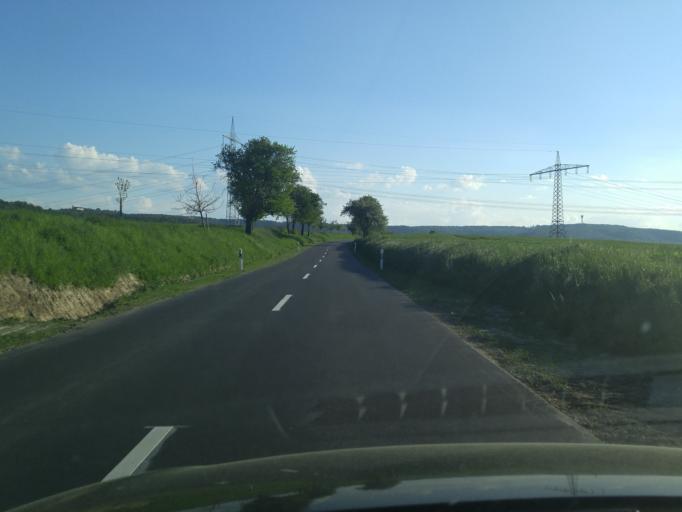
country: DE
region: Baden-Wuerttemberg
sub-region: Regierungsbezirk Stuttgart
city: Brackenheim
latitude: 49.0621
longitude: 9.0549
